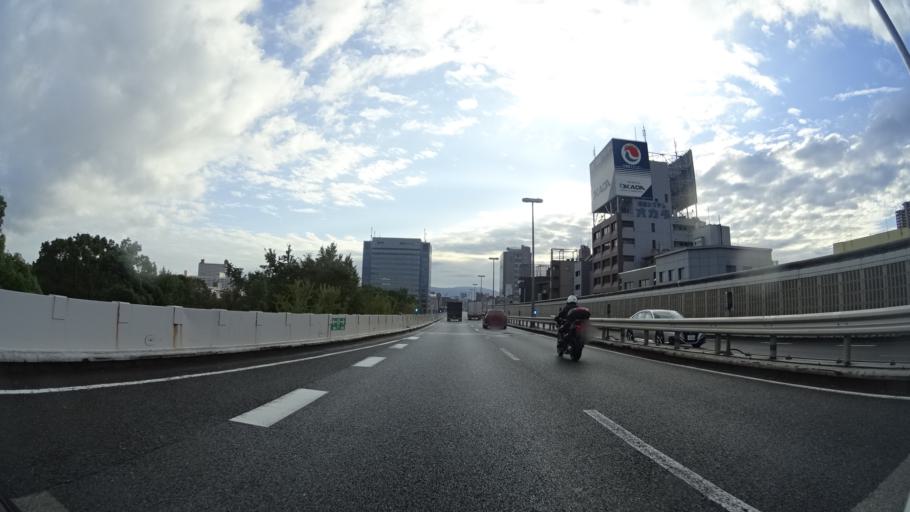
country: JP
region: Osaka
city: Osaka-shi
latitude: 34.6815
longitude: 135.5311
